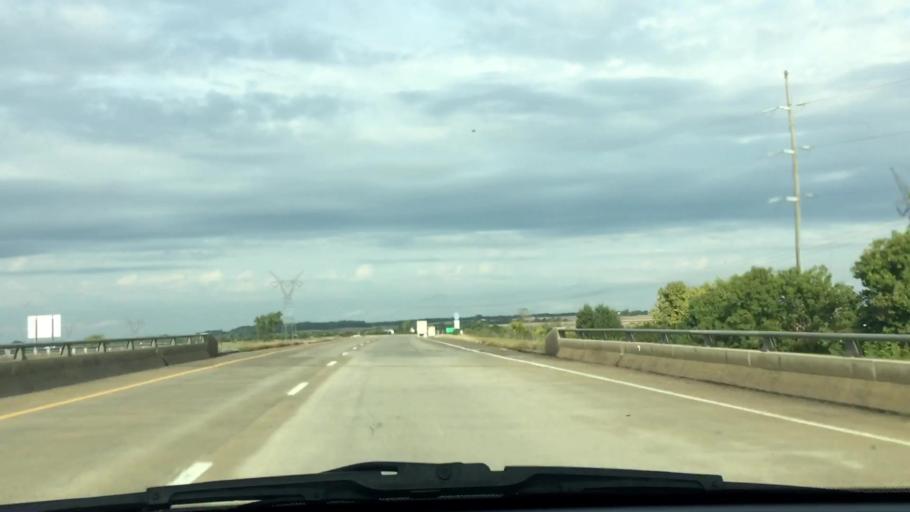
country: US
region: Illinois
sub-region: Whiteside County
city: Sterling
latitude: 41.7616
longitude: -89.7891
